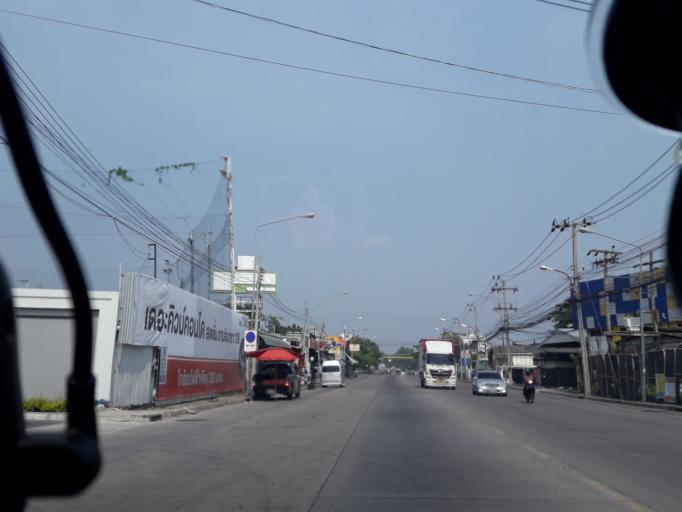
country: TH
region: Bangkok
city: Khan Na Yao
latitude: 13.8151
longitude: 100.6991
